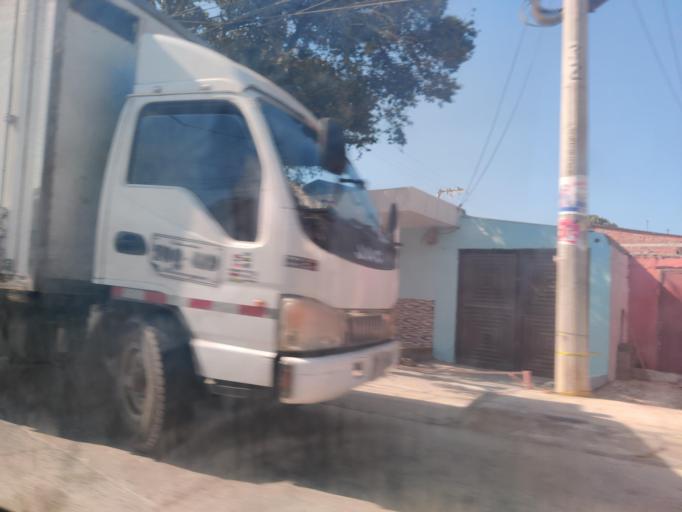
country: CO
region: Atlantico
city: Puerto Colombia
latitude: 10.9873
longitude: -74.9520
